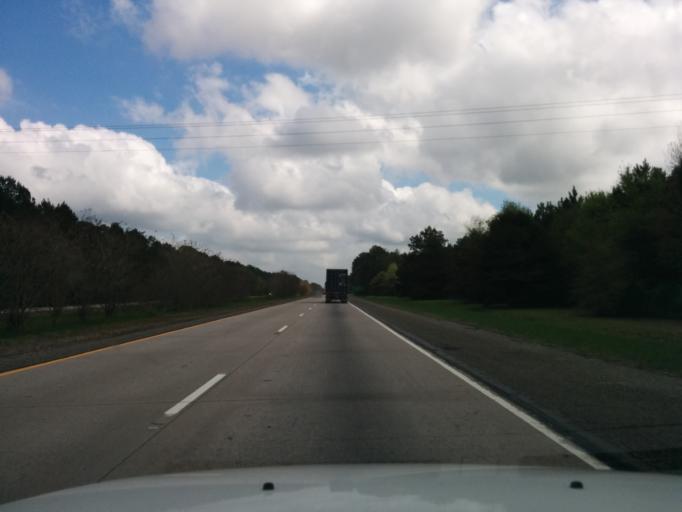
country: US
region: Georgia
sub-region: Bryan County
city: Pembroke
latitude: 32.2304
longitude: -81.6339
